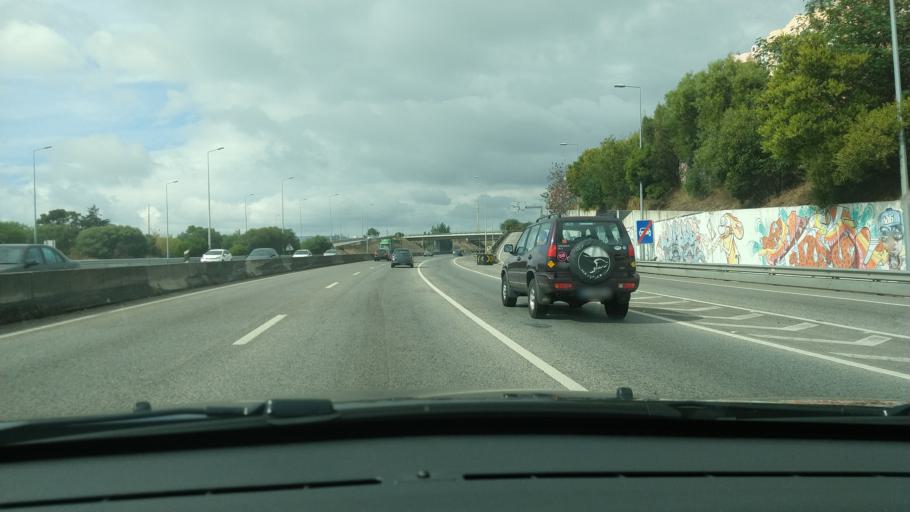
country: PT
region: Lisbon
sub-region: Sintra
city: Cacem
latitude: 38.7665
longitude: -9.3125
